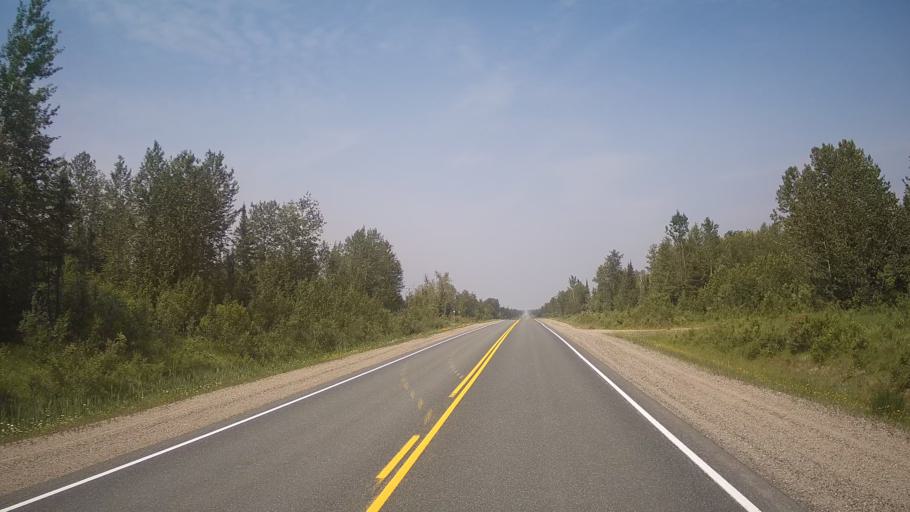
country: CA
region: Ontario
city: Timmins
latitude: 48.7750
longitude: -81.3634
